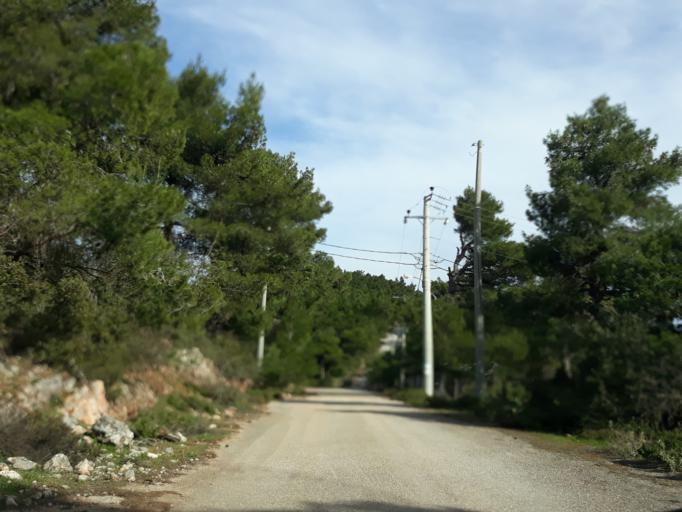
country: GR
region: Attica
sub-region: Nomarchia Anatolikis Attikis
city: Afidnes
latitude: 38.2172
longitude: 23.7999
